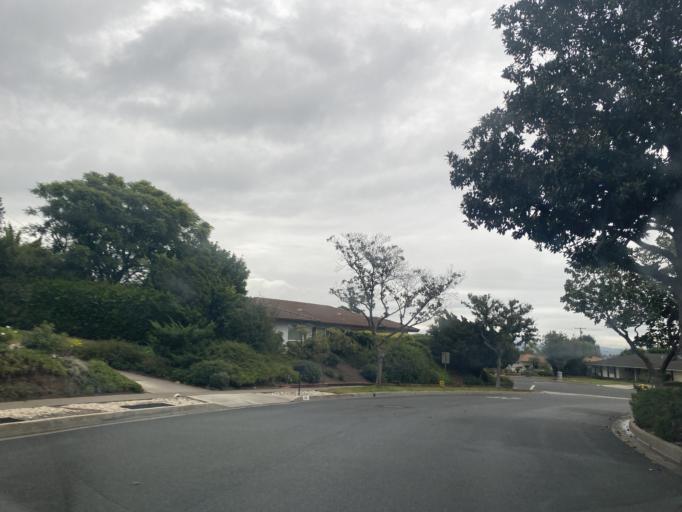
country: US
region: California
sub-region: Orange County
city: Fullerton
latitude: 33.8825
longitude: -117.9133
